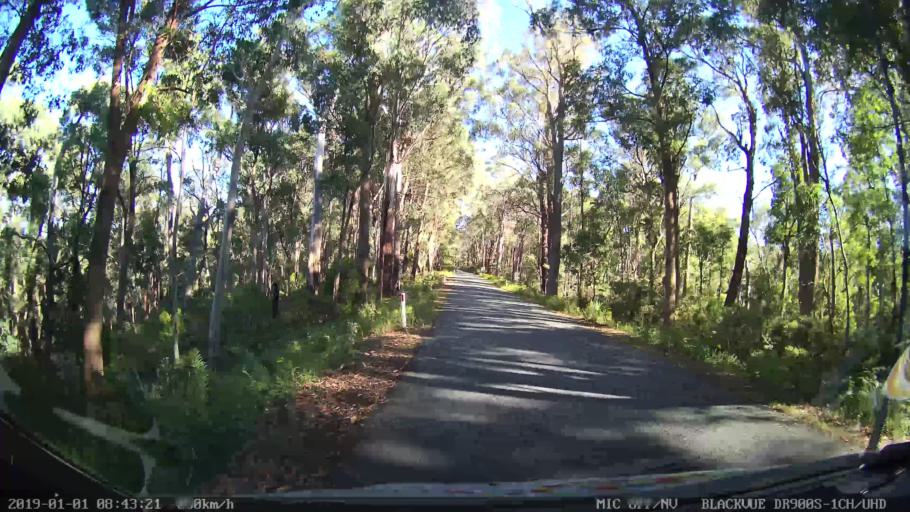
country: AU
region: New South Wales
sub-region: Snowy River
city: Jindabyne
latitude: -36.3179
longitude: 148.1933
